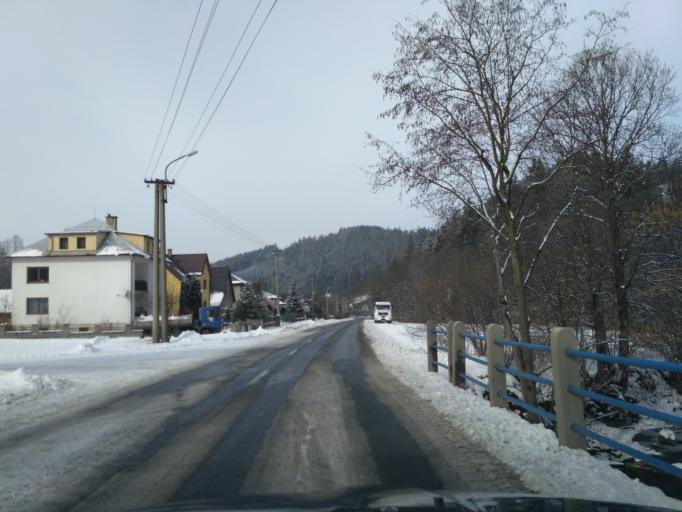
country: CZ
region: Zlin
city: Valasska Bystrice
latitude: 49.4176
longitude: 18.1033
